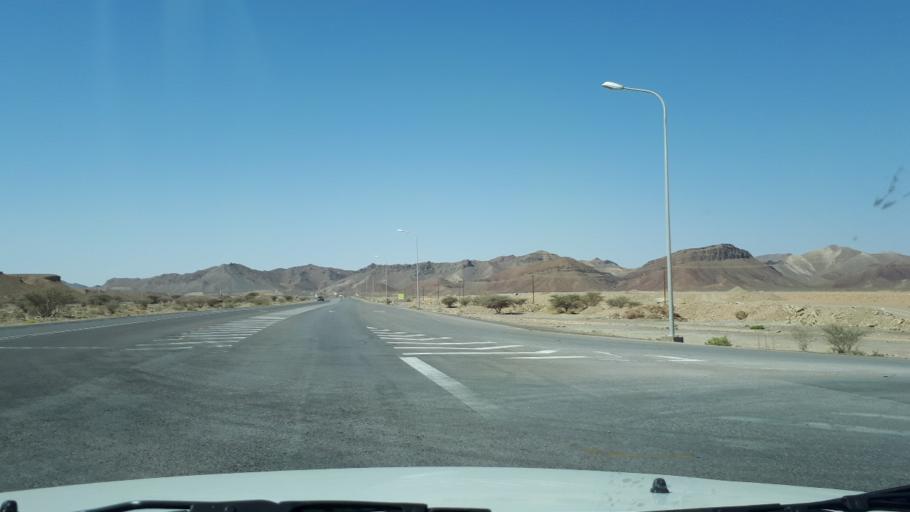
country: OM
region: Ash Sharqiyah
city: Sur
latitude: 22.3728
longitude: 59.3183
